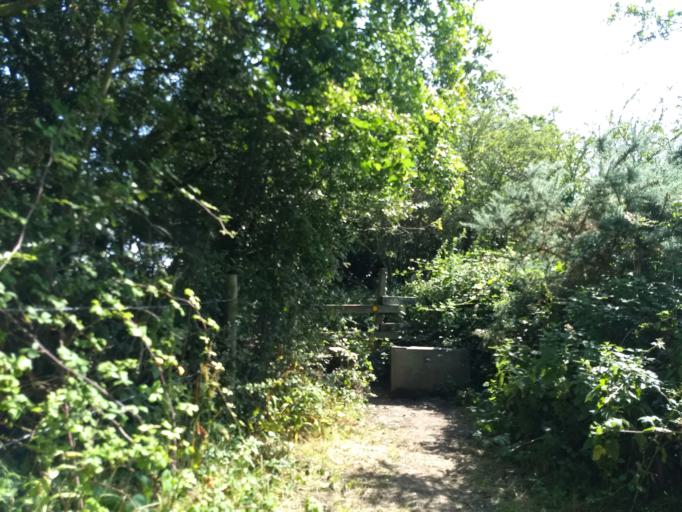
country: GB
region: England
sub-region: Isle of Wight
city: Northwood
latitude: 50.7318
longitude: -1.3115
